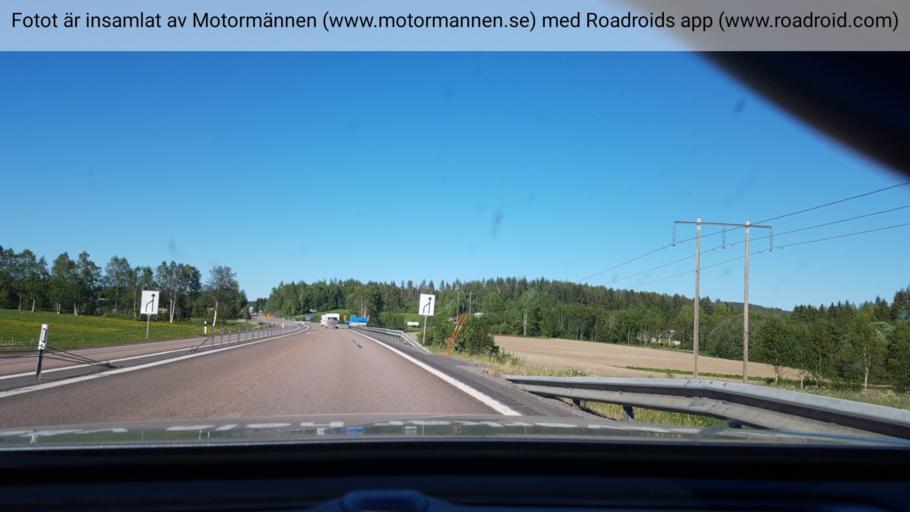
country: SE
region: Vaesternorrland
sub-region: Haernoesands Kommun
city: Haernoesand
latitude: 62.5859
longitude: 17.7817
